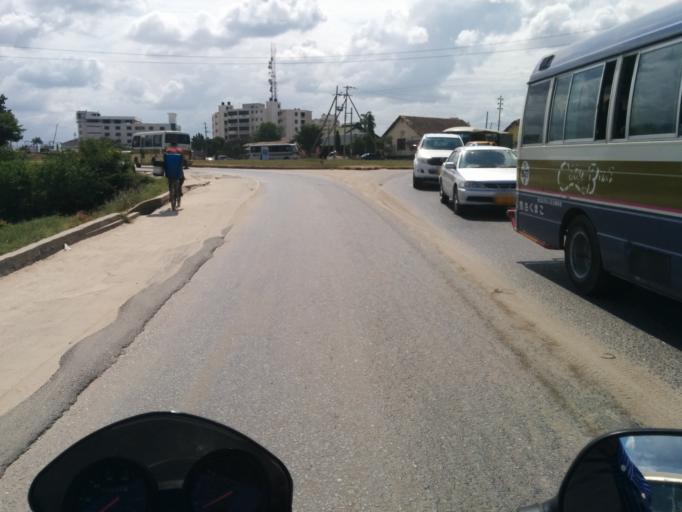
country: TZ
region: Dar es Salaam
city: Dar es Salaam
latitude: -6.8300
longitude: 39.2798
